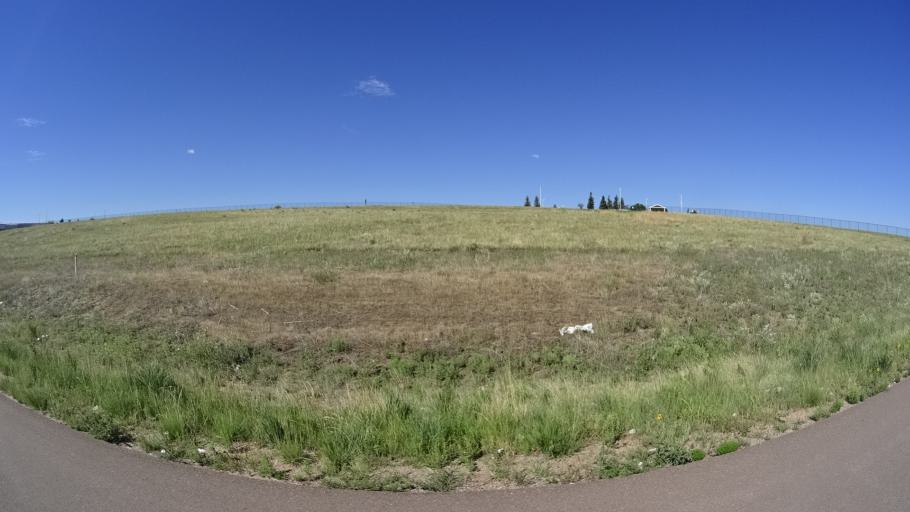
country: US
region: Colorado
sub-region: El Paso County
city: Cimarron Hills
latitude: 38.8175
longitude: -104.6767
